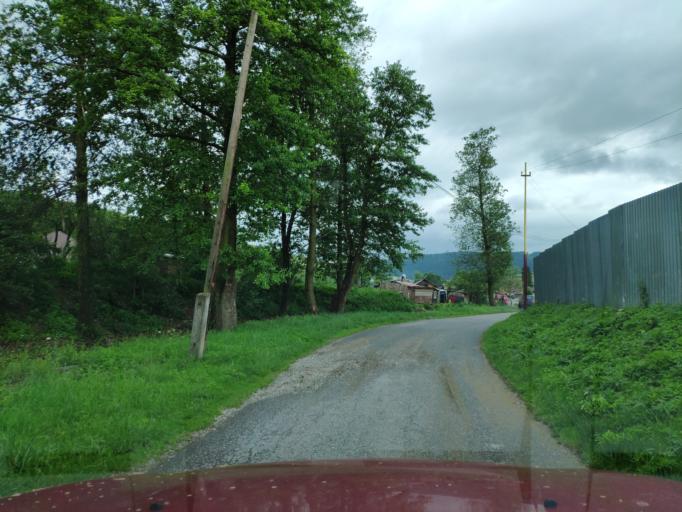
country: SK
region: Presovsky
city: Sabinov
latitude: 49.0424
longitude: 21.0182
